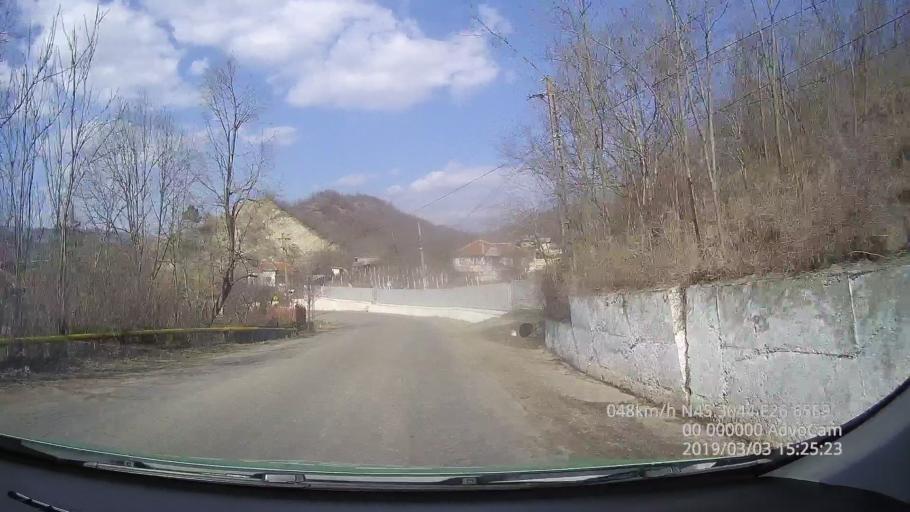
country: RO
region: Buzau
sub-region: Comuna Berca
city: Berca
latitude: 45.3046
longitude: 26.6588
